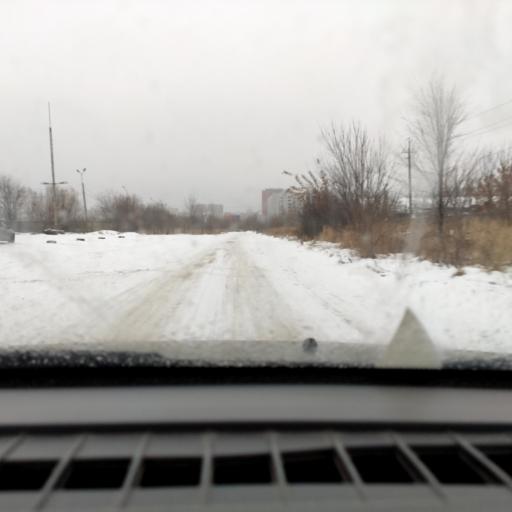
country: RU
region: Samara
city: Tol'yatti
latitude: 53.5533
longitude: 49.3283
